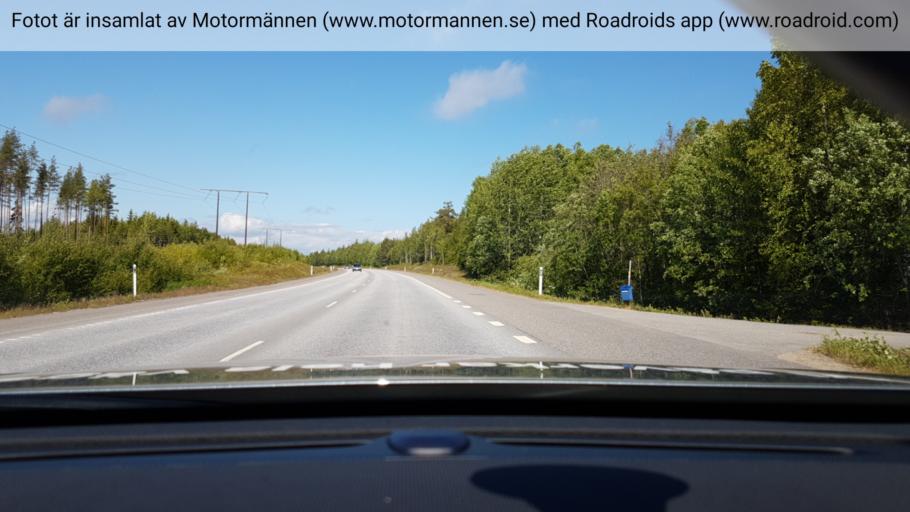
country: SE
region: Vaesterbotten
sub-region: Umea Kommun
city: Holmsund
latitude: 63.7473
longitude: 20.3785
